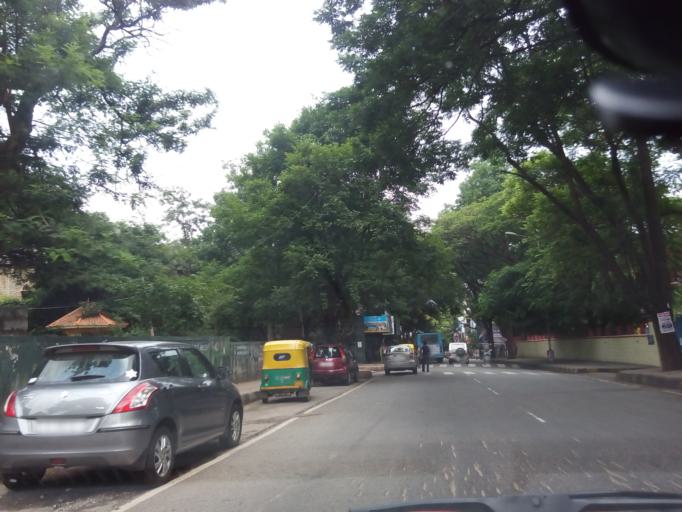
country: IN
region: Karnataka
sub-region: Bangalore Urban
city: Bangalore
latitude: 13.0098
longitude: 77.5691
